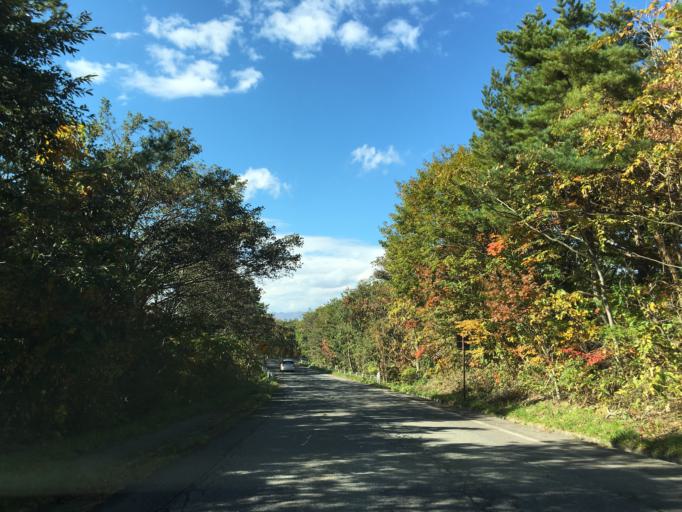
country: JP
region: Fukushima
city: Inawashiro
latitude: 37.6078
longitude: 140.2313
